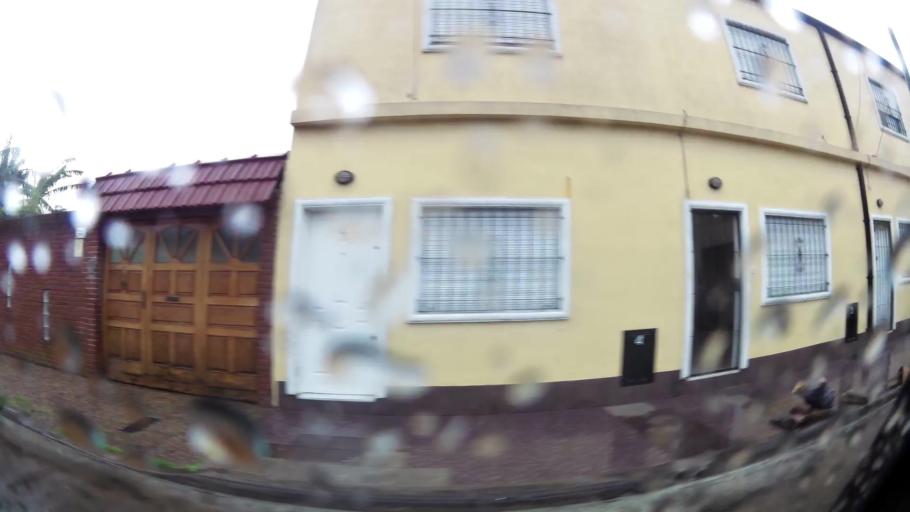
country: AR
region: Buenos Aires
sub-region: Partido de Lanus
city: Lanus
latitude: -34.7166
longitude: -58.4027
